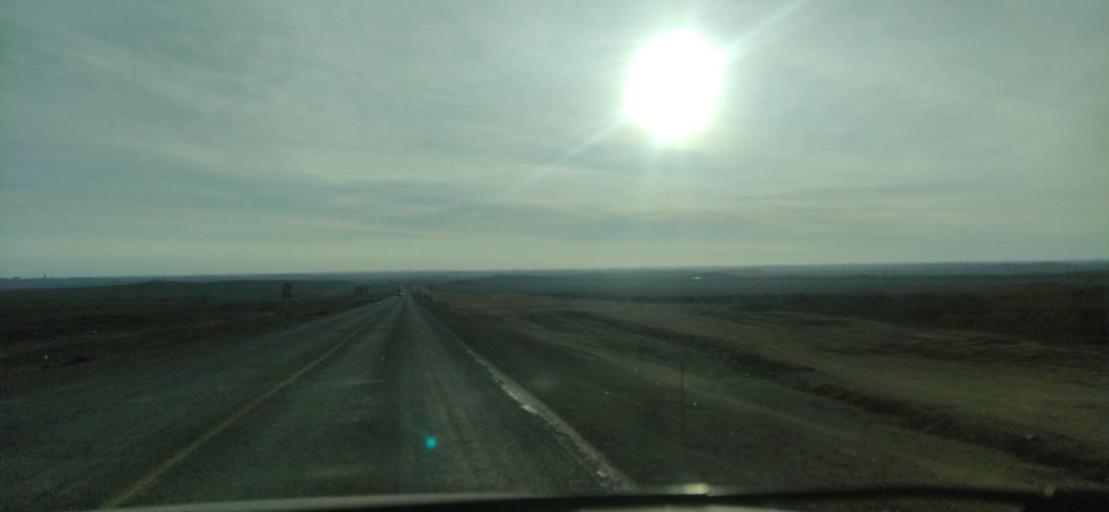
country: KZ
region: Qaraghandy
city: Saryshaghan
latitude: 46.1636
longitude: 73.6144
